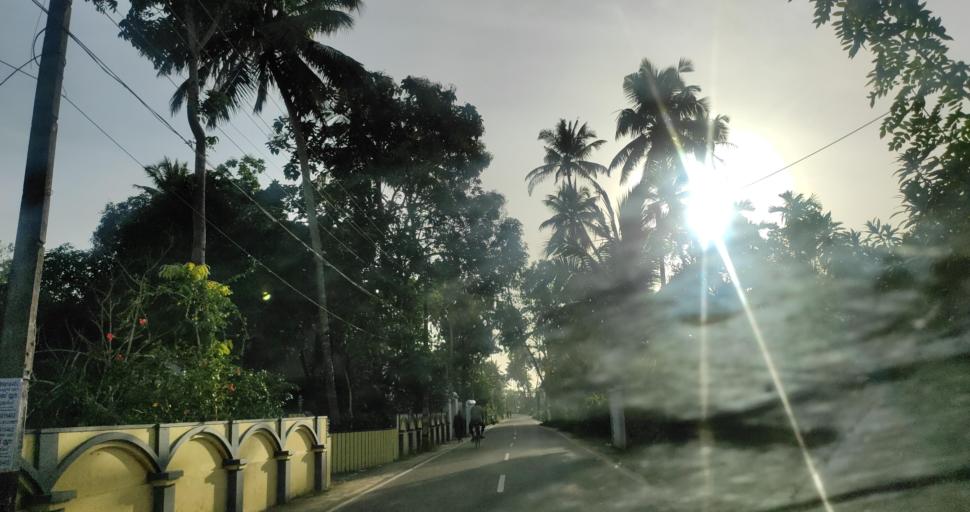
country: IN
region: Kerala
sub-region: Alappuzha
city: Shertallai
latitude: 9.6018
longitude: 76.3023
